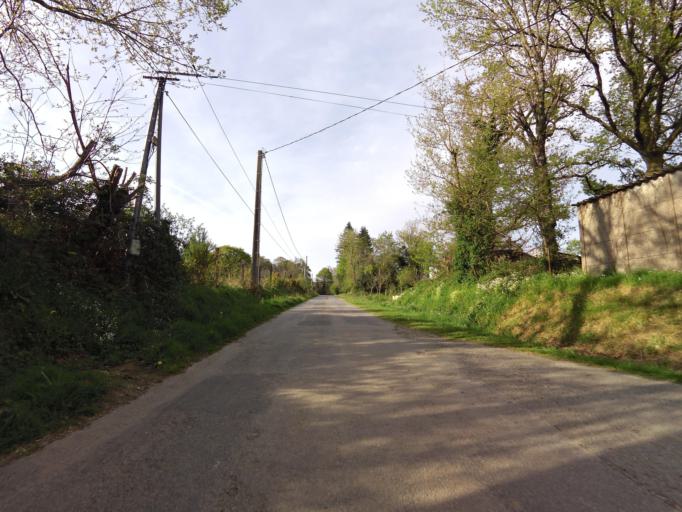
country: FR
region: Brittany
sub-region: Departement du Morbihan
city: Pluherlin
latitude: 47.7199
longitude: -2.3703
